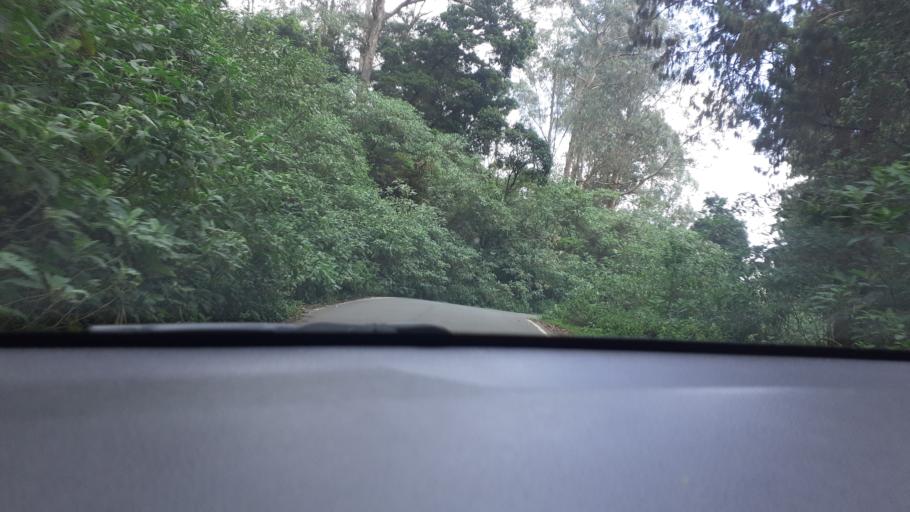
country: IN
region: Tamil Nadu
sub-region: Dindigul
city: Kodaikanal
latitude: 10.2430
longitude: 77.4211
